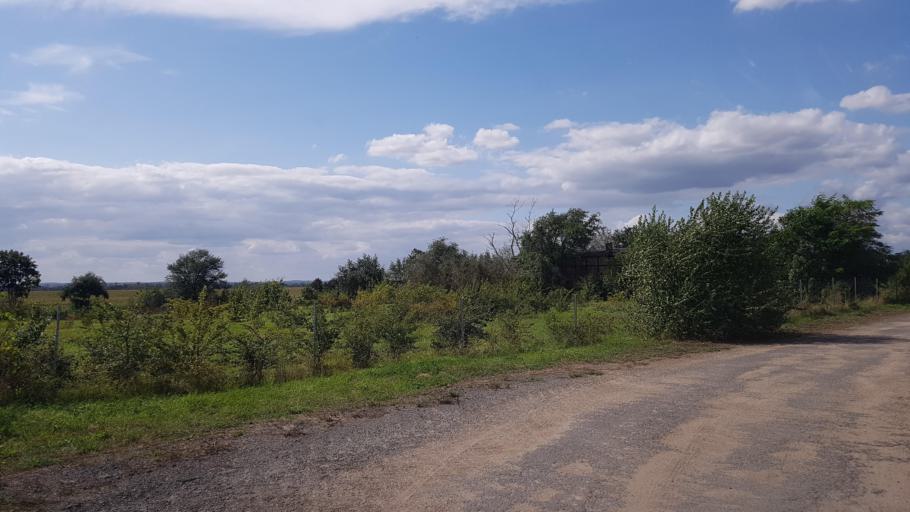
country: DE
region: Brandenburg
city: Muhlberg
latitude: 51.4276
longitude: 13.2631
